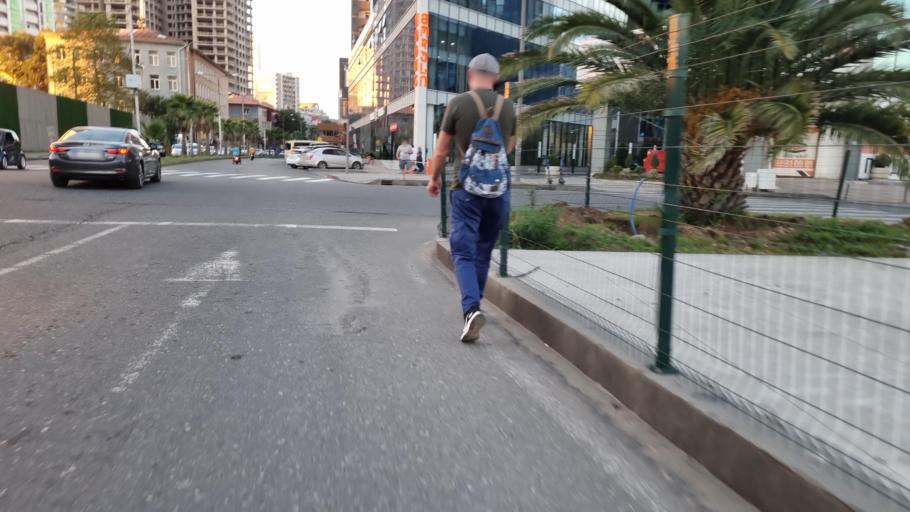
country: GE
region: Ajaria
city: Batumi
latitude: 41.6393
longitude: 41.6161
